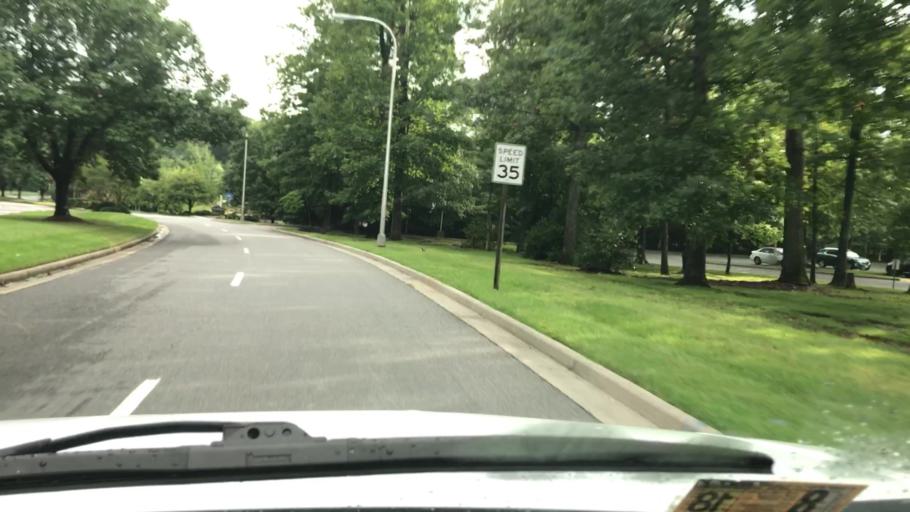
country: US
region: Virginia
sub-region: Henrico County
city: Short Pump
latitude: 37.6103
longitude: -77.6673
